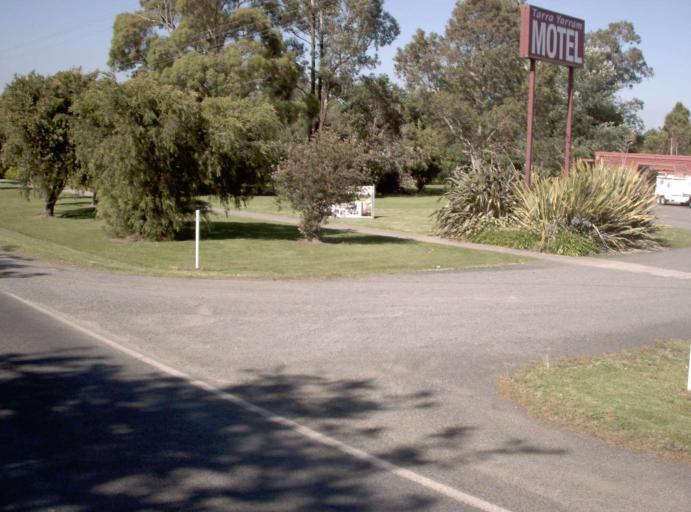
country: AU
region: Victoria
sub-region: Latrobe
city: Traralgon
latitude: -38.5701
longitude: 146.6745
